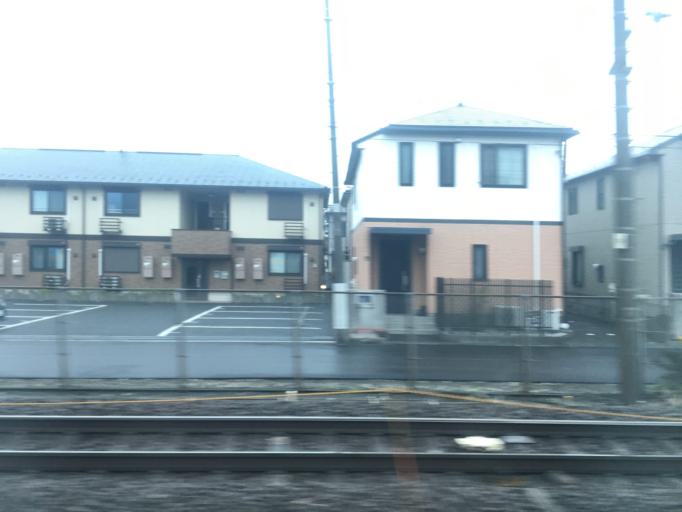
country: JP
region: Tokyo
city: Hino
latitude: 35.6618
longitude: 139.3850
